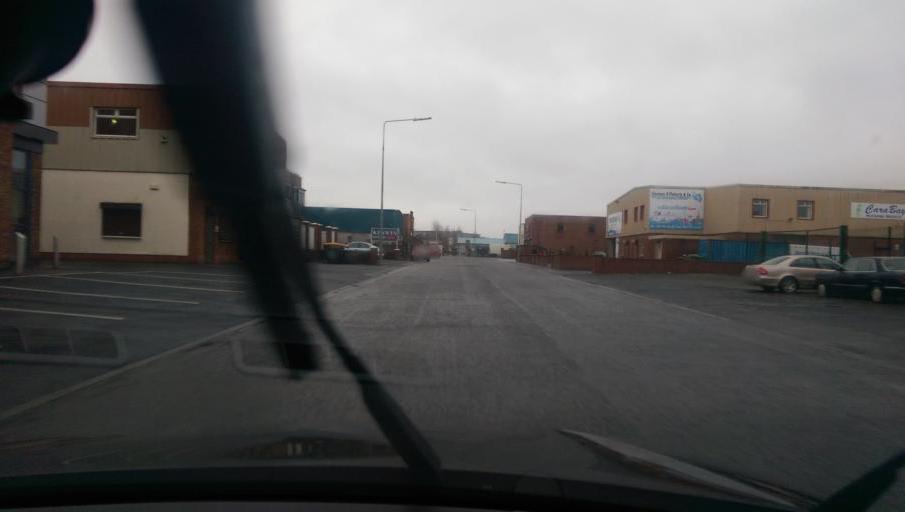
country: IE
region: Connaught
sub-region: County Galway
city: Gaillimh
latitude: 53.2863
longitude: -9.0377
